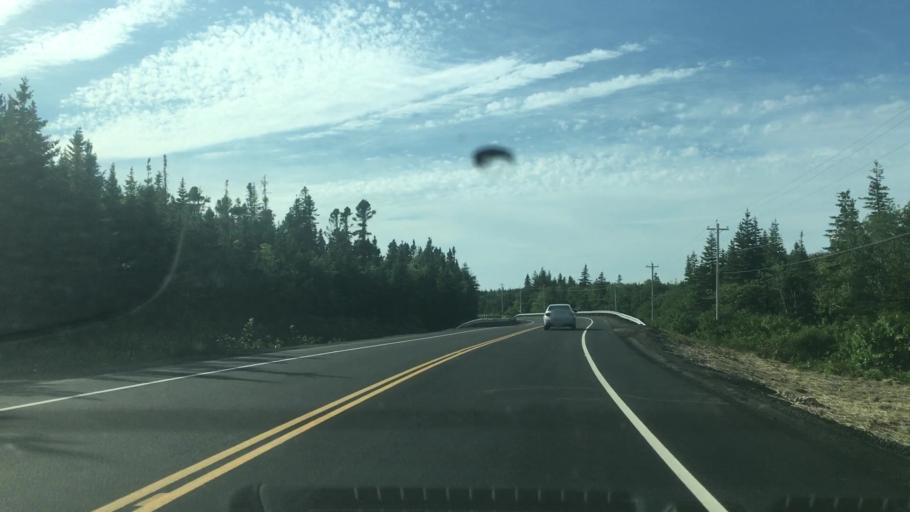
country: CA
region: Nova Scotia
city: Sydney Mines
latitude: 46.8408
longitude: -60.3916
